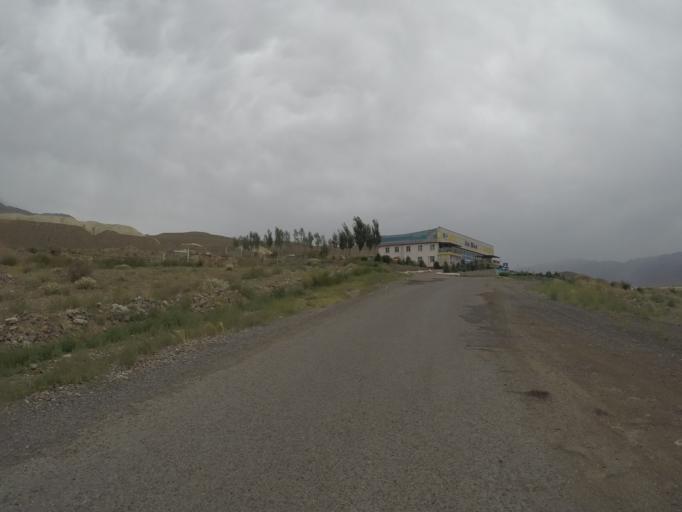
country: KG
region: Naryn
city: Kochkor
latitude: 42.5098
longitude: 75.8324
